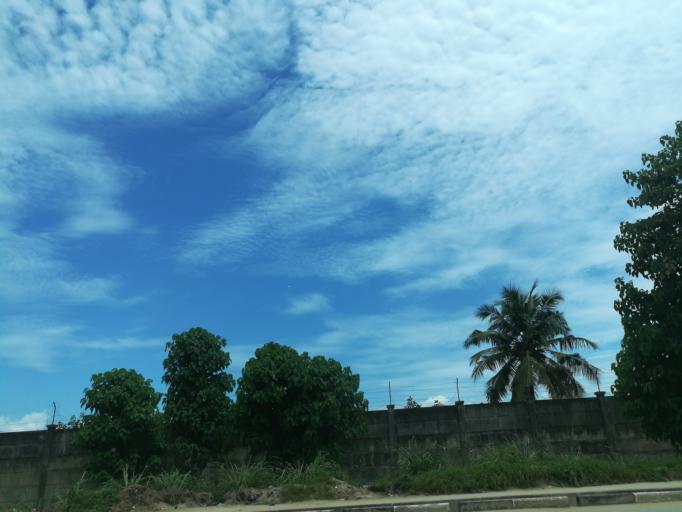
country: NG
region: Lagos
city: Ebute Ikorodu
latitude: 6.5709
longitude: 3.4829
